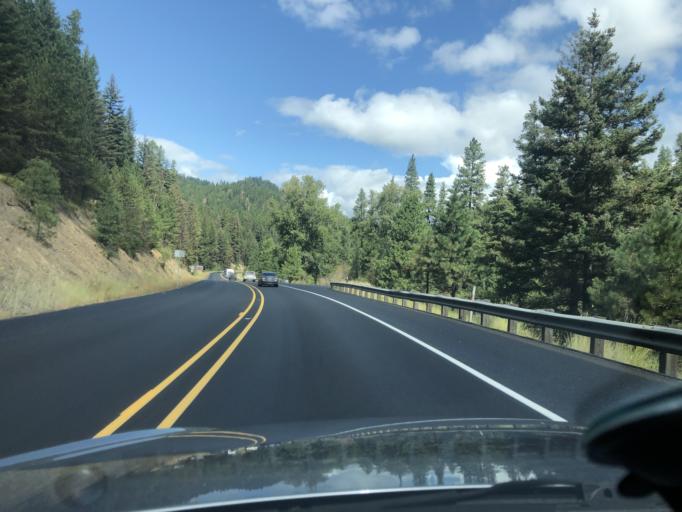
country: US
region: Washington
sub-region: Kittitas County
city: Cle Elum
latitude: 47.2950
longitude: -120.7000
